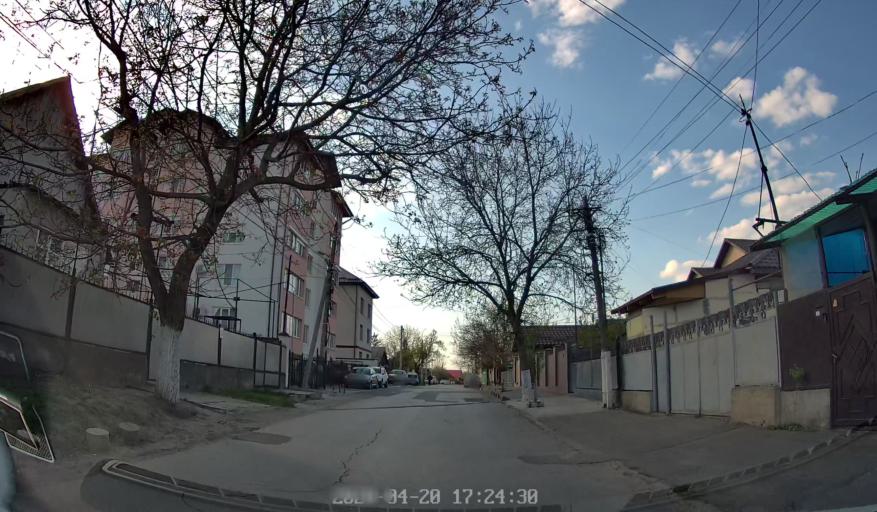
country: MD
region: Chisinau
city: Chisinau
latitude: 46.9906
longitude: 28.8791
